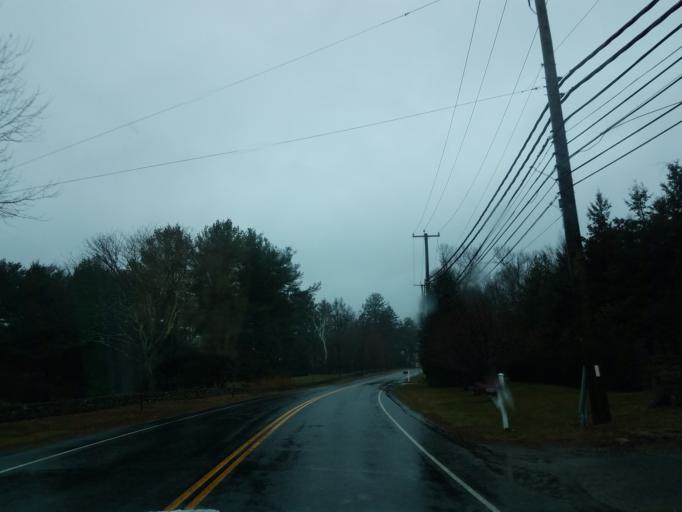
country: US
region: Connecticut
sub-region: Fairfield County
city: Westport
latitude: 41.1223
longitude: -73.3243
